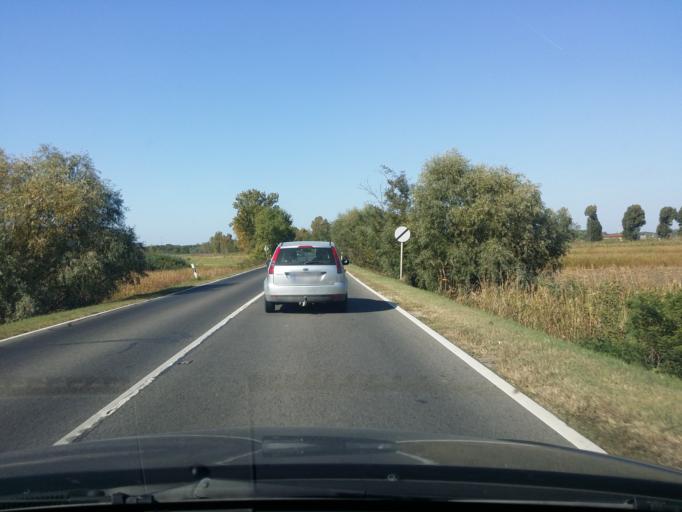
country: HU
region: Bacs-Kiskun
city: Lakitelek
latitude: 46.8702
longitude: 20.0379
